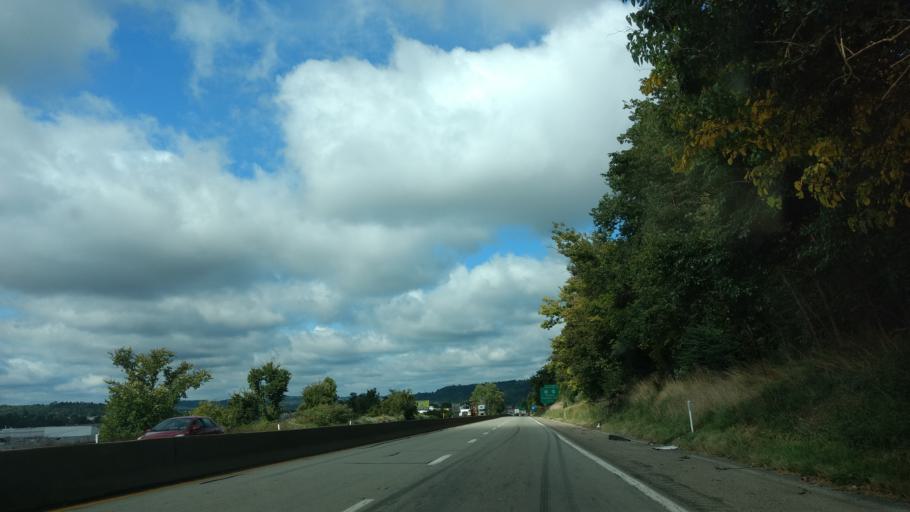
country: US
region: Pennsylvania
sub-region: Westmoreland County
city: Lynnwood-Pricedale
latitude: 40.1399
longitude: -79.8289
